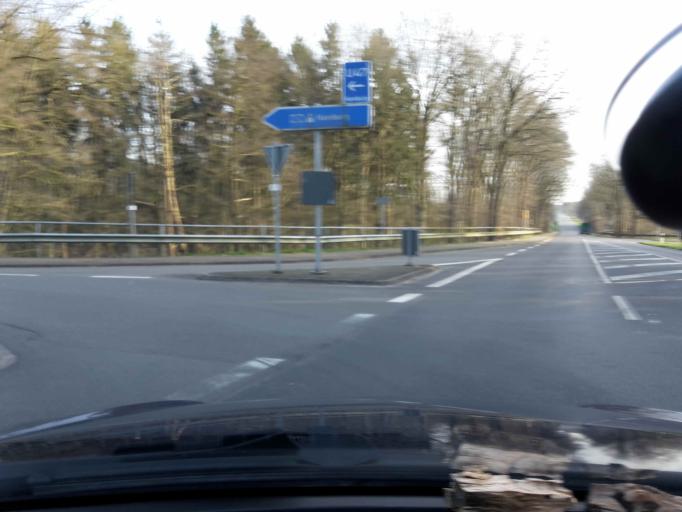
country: DE
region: Lower Saxony
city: Hollenstedt
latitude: 53.3578
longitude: 9.7104
